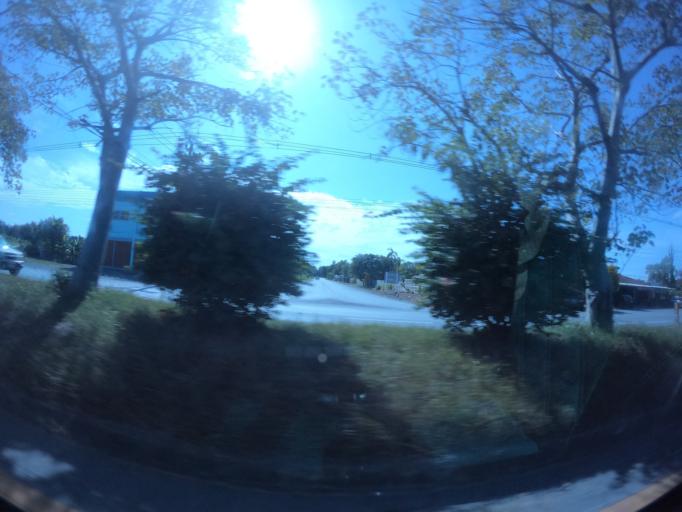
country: TH
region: Nakhon Nayok
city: Ban Na
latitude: 14.2412
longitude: 101.0713
